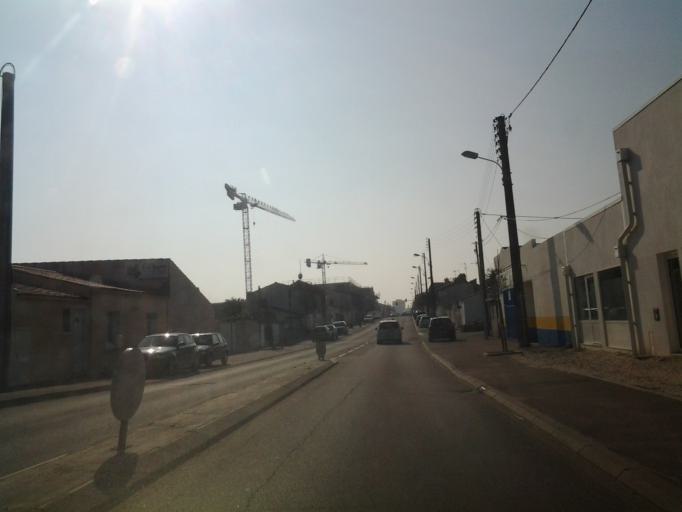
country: FR
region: Pays de la Loire
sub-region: Departement de la Vendee
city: Les Sables-d'Olonne
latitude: 46.5059
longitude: -1.7714
